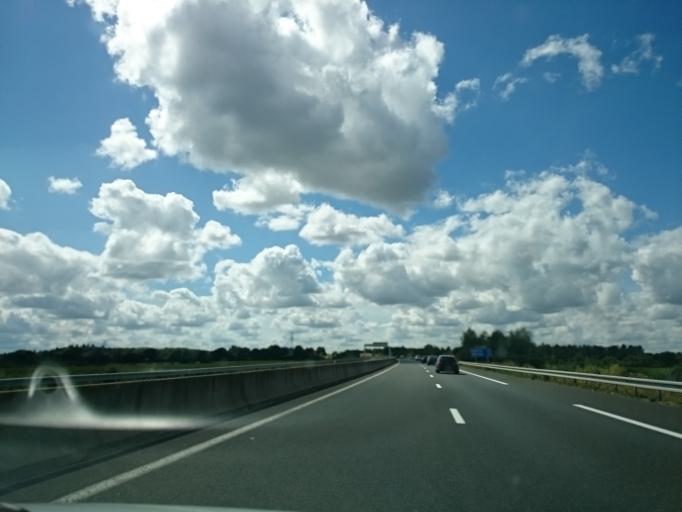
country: FR
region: Pays de la Loire
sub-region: Departement de Maine-et-Loire
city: Beaucouze
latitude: 47.4919
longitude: -0.6431
